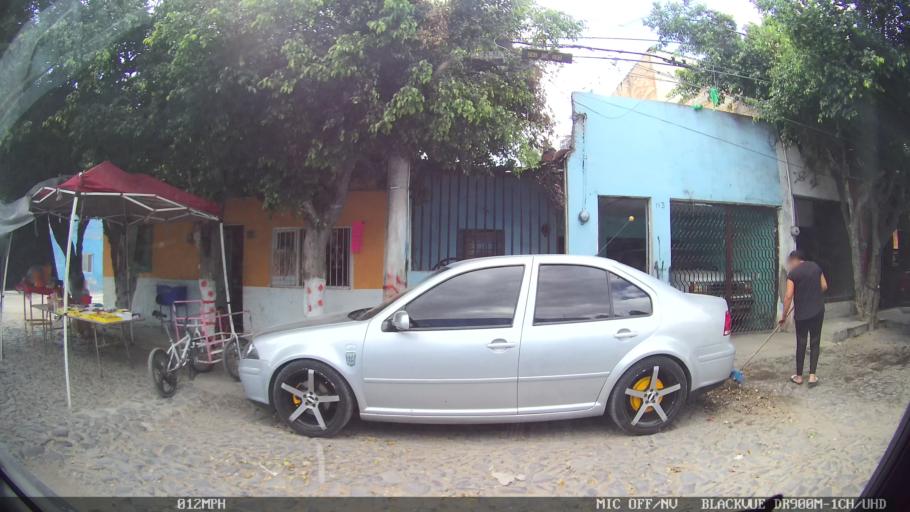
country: MX
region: Jalisco
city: Tlaquepaque
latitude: 20.6825
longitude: -103.2614
